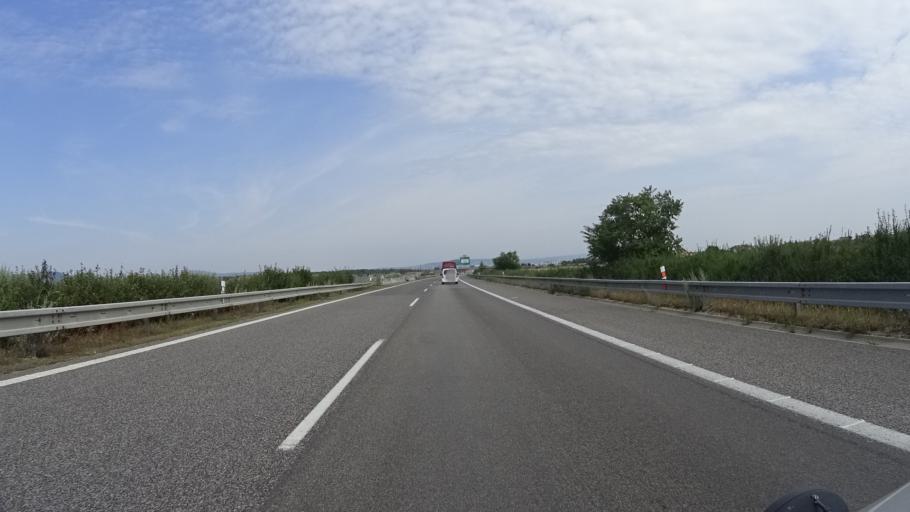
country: AT
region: Burgenland
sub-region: Politischer Bezirk Neusiedl am See
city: Deutsch Jahrndorf
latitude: 48.0627
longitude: 17.1020
